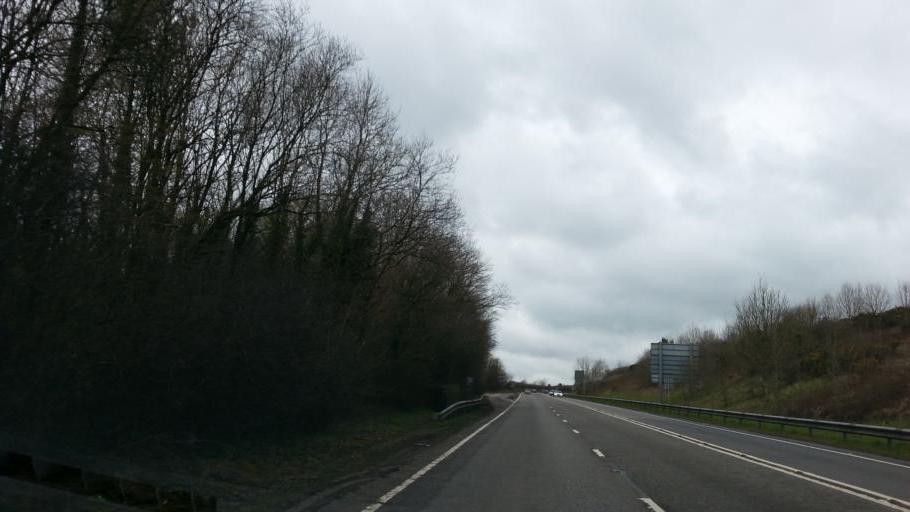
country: GB
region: England
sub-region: Devon
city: South Molton
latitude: 51.0388
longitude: -3.8574
